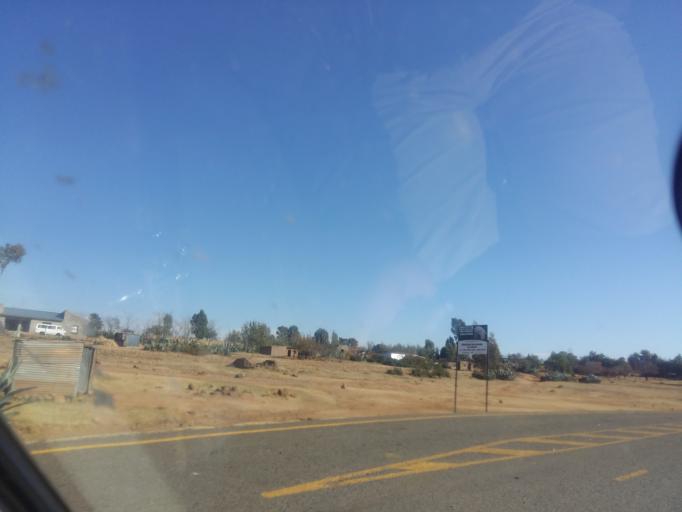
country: LS
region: Mafeteng
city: Mafeteng
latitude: -29.6619
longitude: 27.2685
